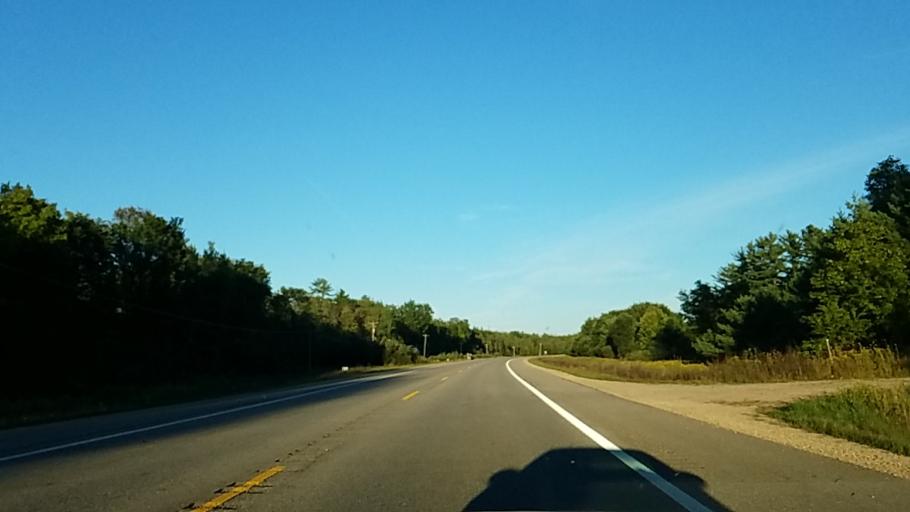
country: US
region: Michigan
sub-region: Alger County
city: Munising
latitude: 46.4424
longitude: -86.7387
